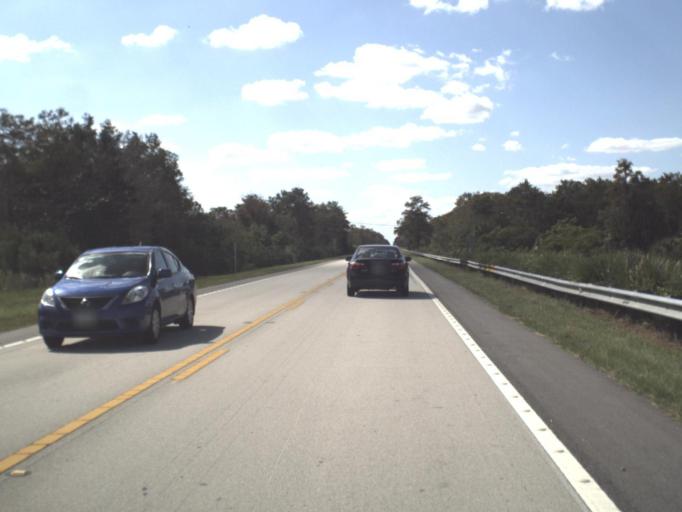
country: US
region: Florida
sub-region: Miami-Dade County
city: Kendall West
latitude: 25.8569
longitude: -81.0336
